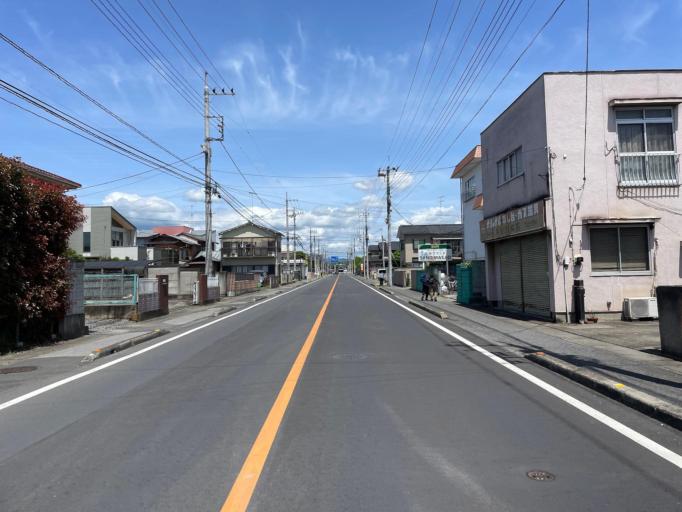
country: JP
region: Tochigi
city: Sano
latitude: 36.3196
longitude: 139.5848
